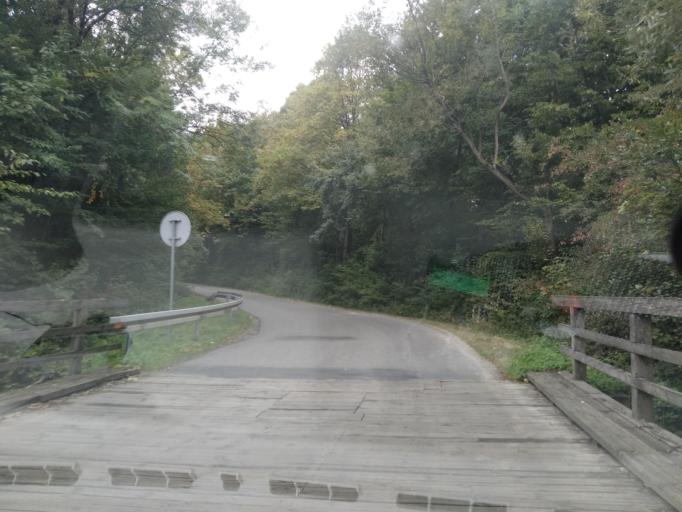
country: PL
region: Lesser Poland Voivodeship
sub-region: Powiat gorlicki
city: Bystra
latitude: 49.6149
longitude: 21.1154
